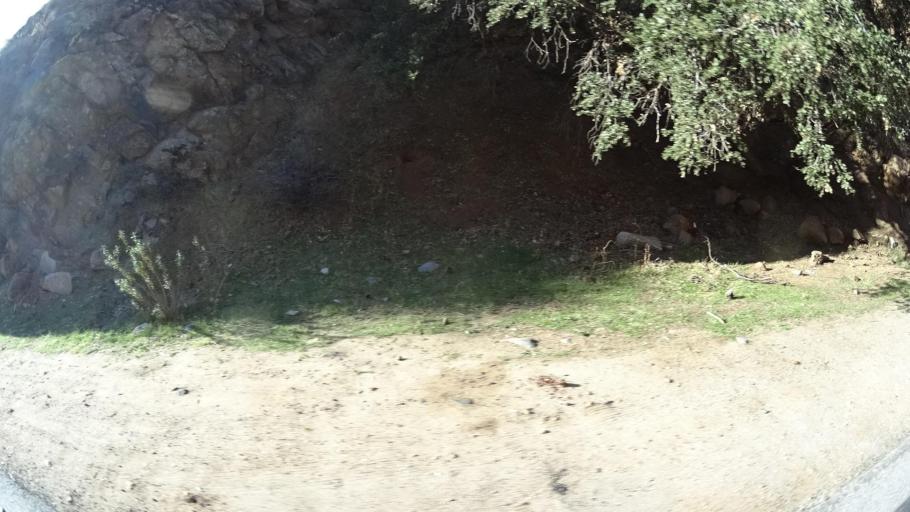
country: US
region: California
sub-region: Kern County
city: Golden Hills
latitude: 35.3154
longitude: -118.5309
